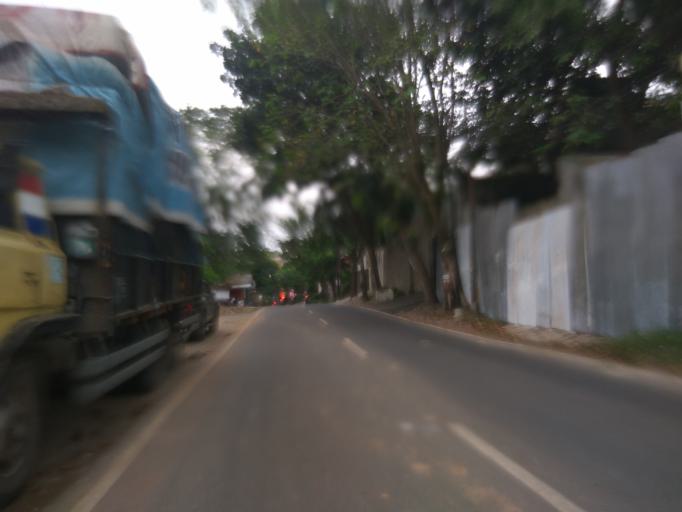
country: ID
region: Central Java
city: Semarang
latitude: -7.0123
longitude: 110.4145
